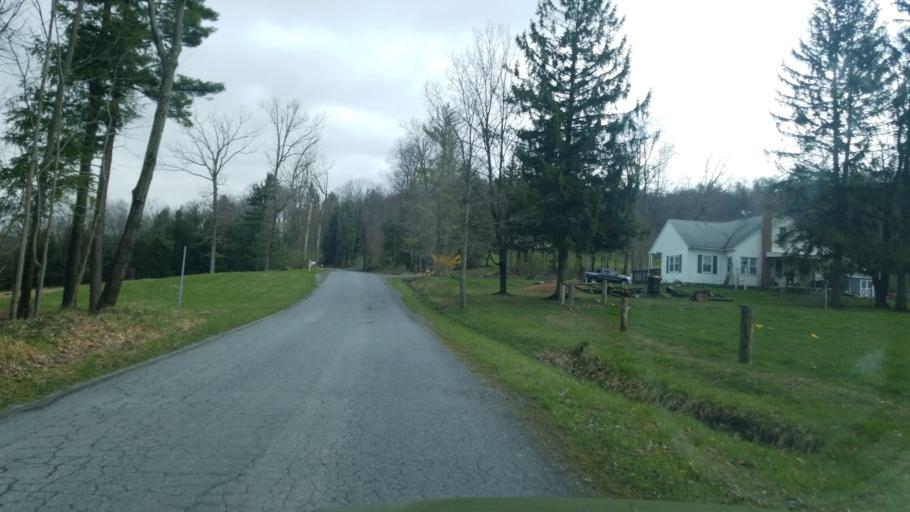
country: US
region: Pennsylvania
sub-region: Clearfield County
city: Shiloh
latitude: 41.1141
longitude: -78.3418
